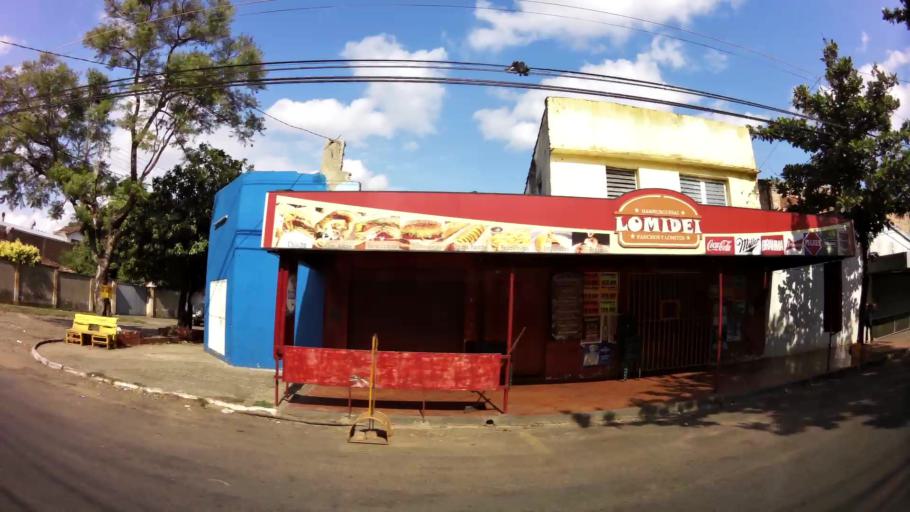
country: PY
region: Central
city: Fernando de la Mora
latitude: -25.3350
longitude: -57.5321
